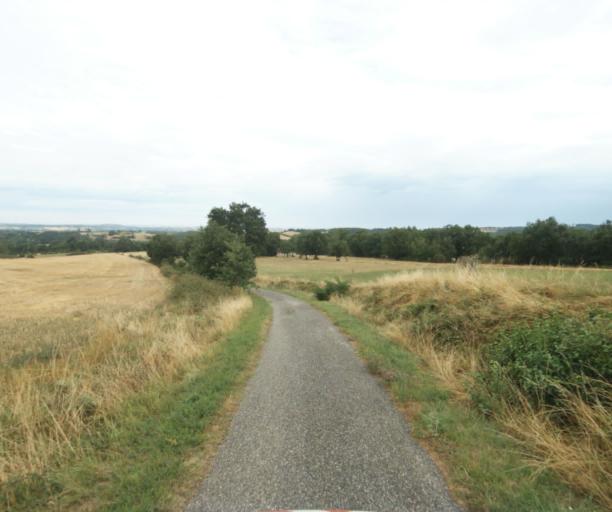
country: FR
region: Midi-Pyrenees
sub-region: Departement de la Haute-Garonne
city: Revel
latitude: 43.4151
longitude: 1.9816
